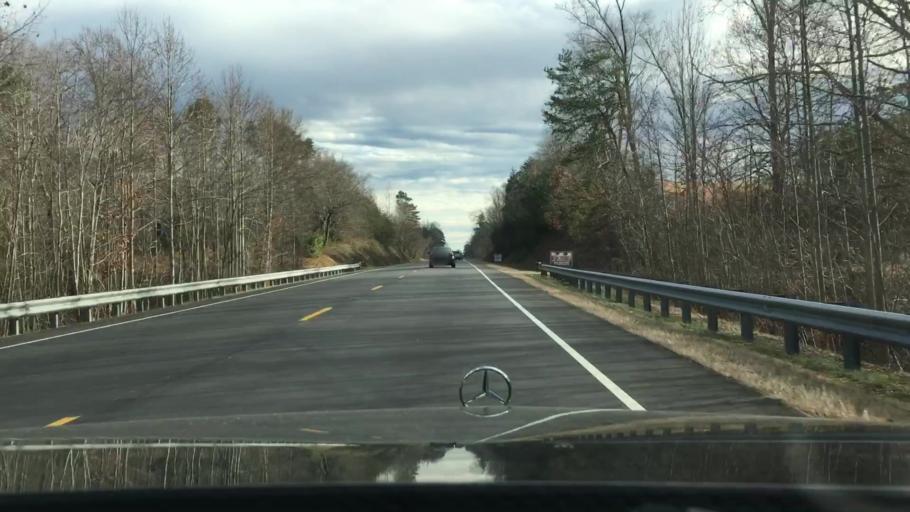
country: US
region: North Carolina
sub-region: Caswell County
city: Yanceyville
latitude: 36.4547
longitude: -79.3693
